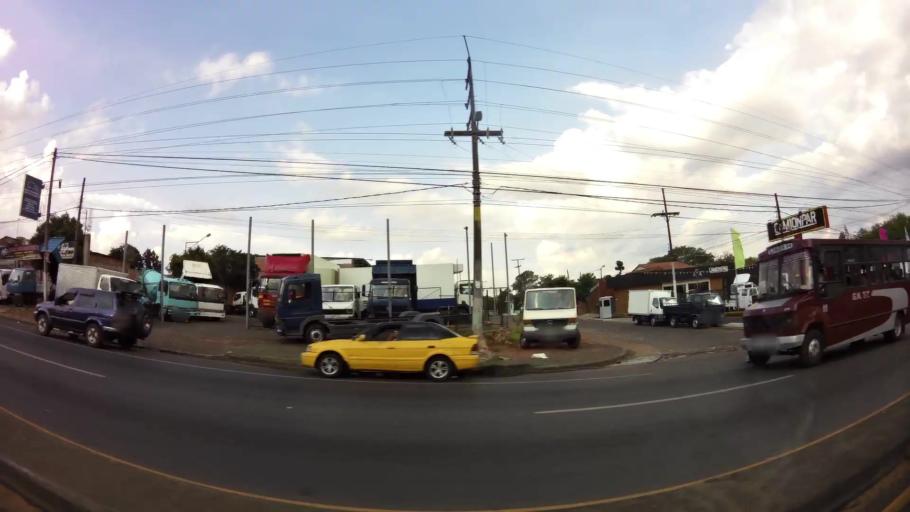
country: PY
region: Central
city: Villa Elisa
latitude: -25.3596
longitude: -57.5677
